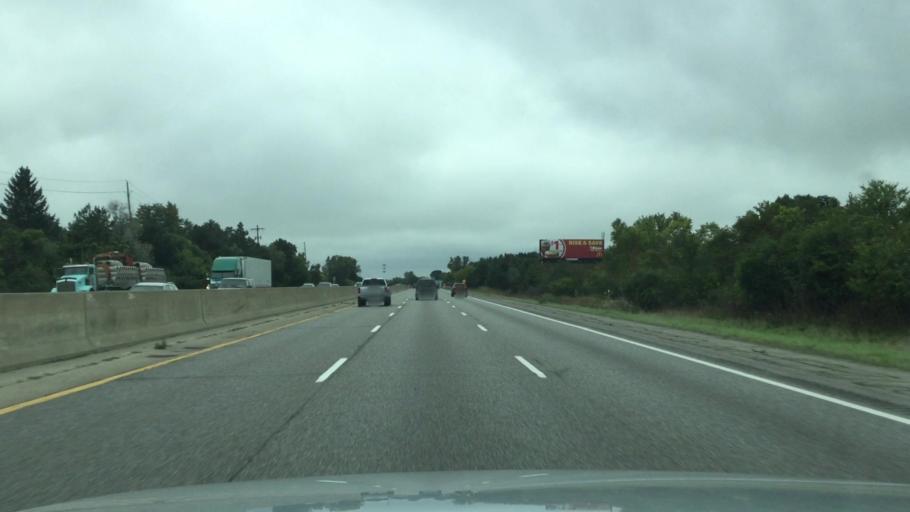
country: US
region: Michigan
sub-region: Genesee County
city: Flint
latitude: 43.0109
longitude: -83.7481
